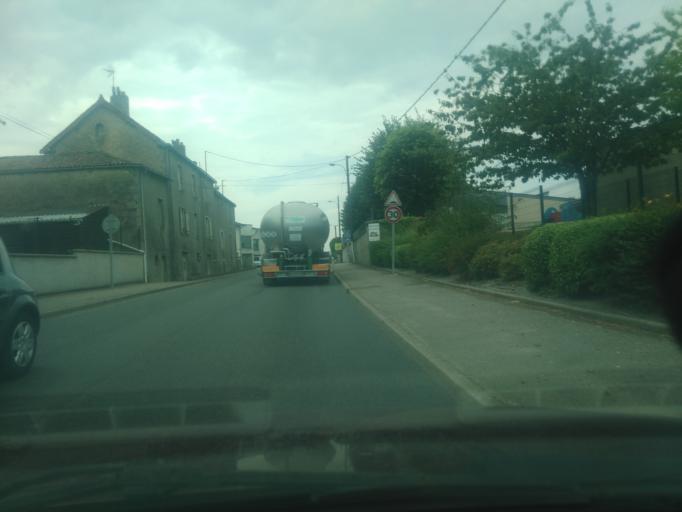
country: FR
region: Poitou-Charentes
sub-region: Departement des Deux-Sevres
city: Secondigny
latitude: 46.6086
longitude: -0.4104
